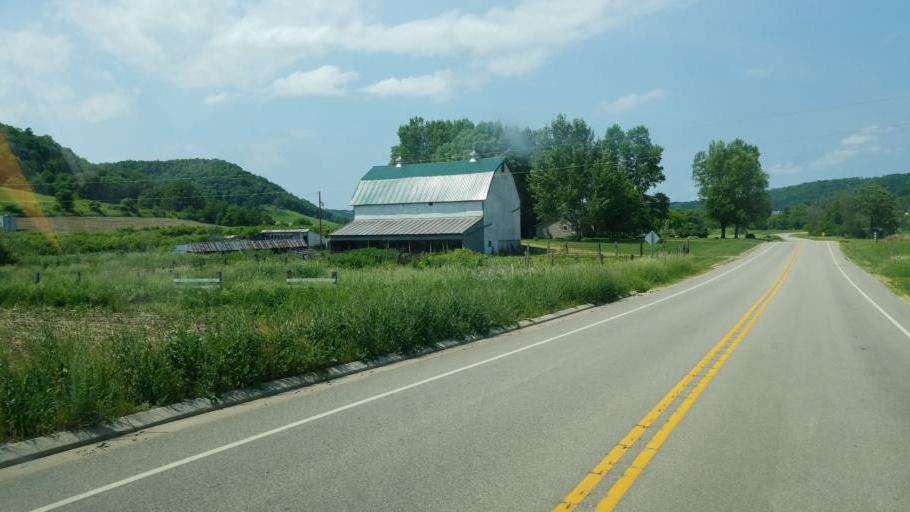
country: US
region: Wisconsin
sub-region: Vernon County
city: Westby
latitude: 43.5426
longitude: -90.6663
